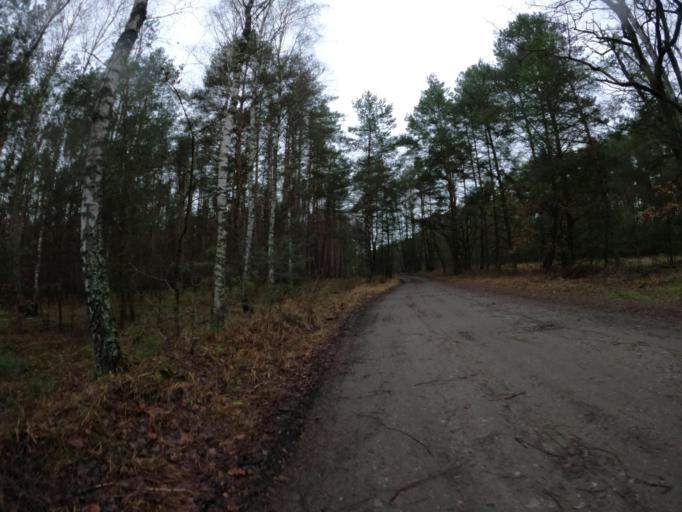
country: PL
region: West Pomeranian Voivodeship
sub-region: Powiat mysliborski
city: Debno
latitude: 52.7953
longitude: 14.7593
